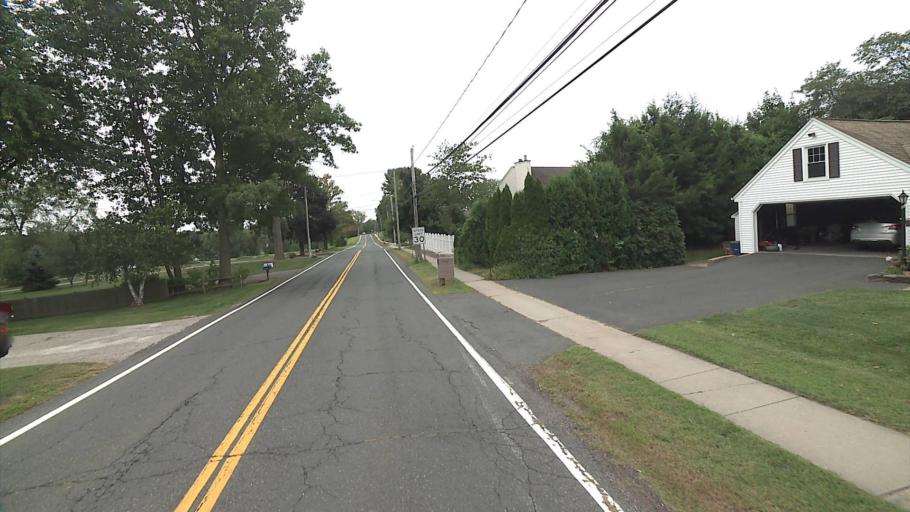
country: US
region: Connecticut
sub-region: Hartford County
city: Manchester
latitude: 41.8030
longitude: -72.4709
